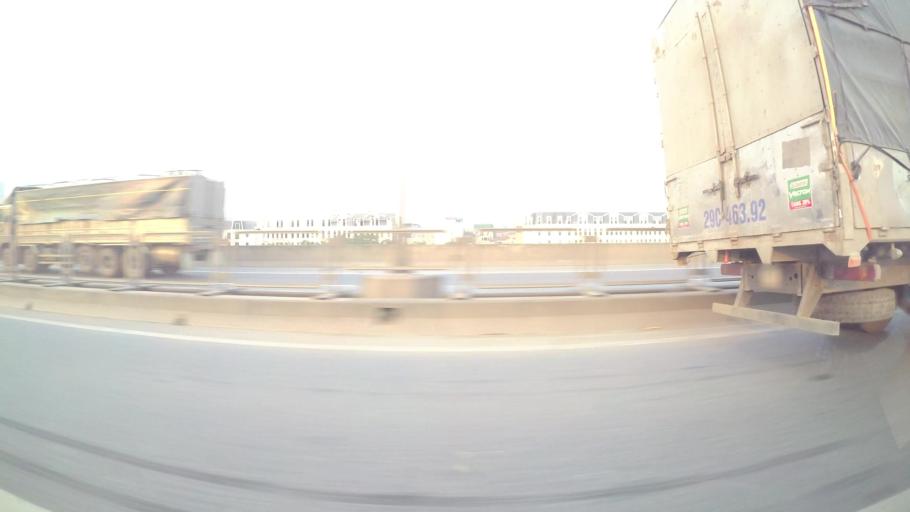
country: VN
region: Ha Noi
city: Thanh Xuan
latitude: 20.9780
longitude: 105.8131
